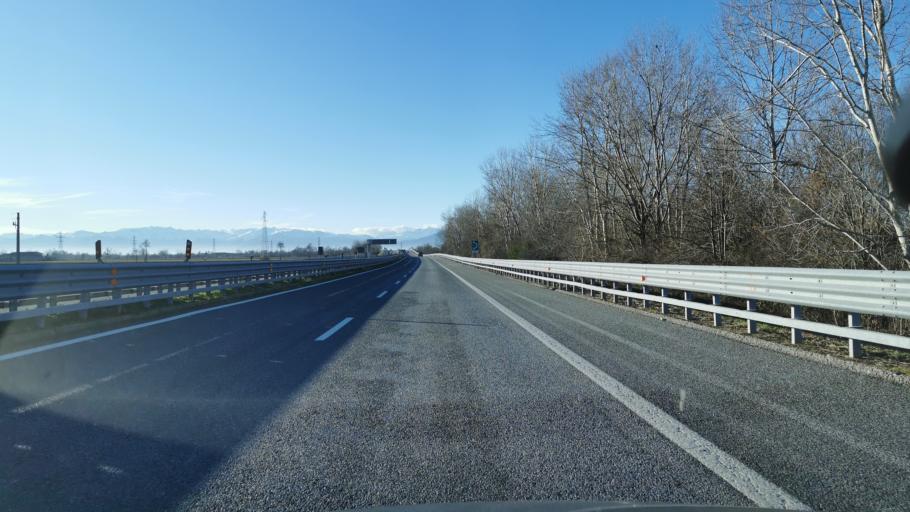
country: IT
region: Piedmont
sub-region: Provincia di Cuneo
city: Trinita
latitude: 44.4692
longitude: 7.7588
